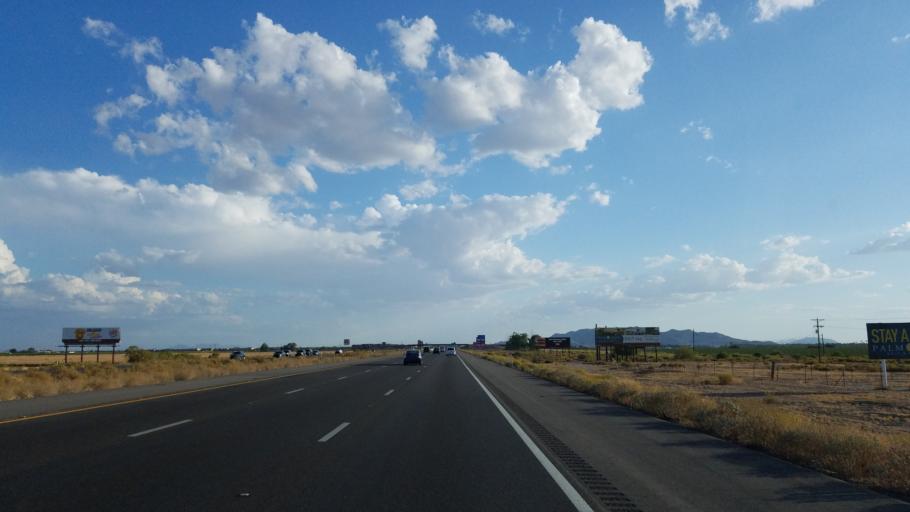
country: US
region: Arizona
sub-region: Pinal County
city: Casa Grande
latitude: 32.9030
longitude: -111.6870
